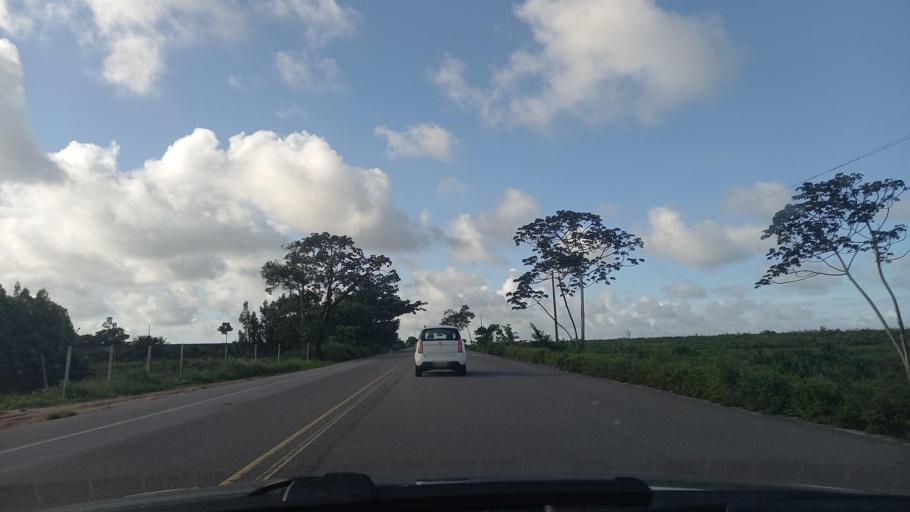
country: BR
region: Alagoas
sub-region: Marechal Deodoro
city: Marechal Deodoro
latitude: -9.8291
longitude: -35.9290
